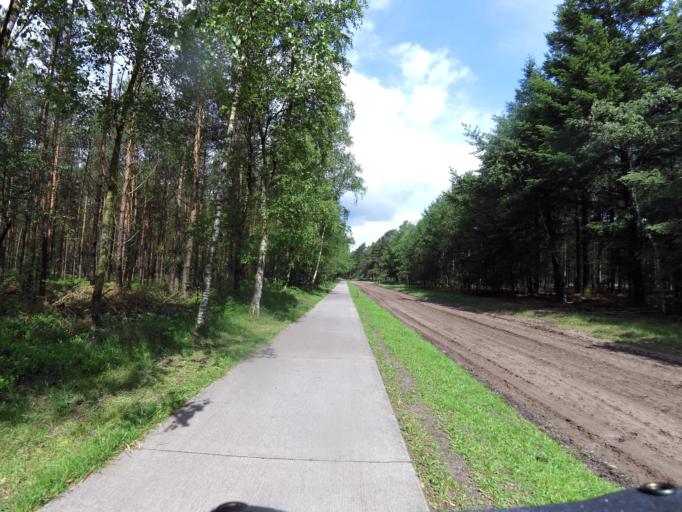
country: NL
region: Gelderland
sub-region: Gemeente Apeldoorn
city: Uddel
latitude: 52.3037
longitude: 5.7769
